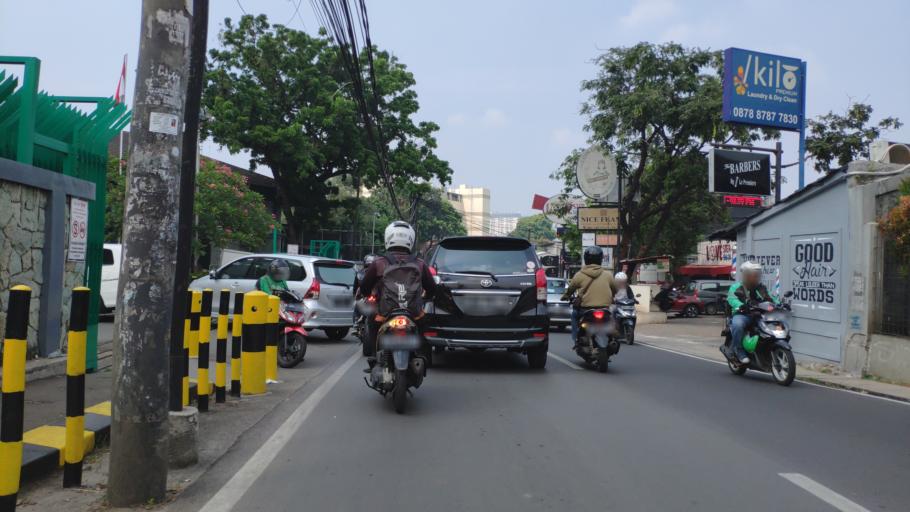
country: ID
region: Banten
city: South Tangerang
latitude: -6.2842
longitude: 106.7891
